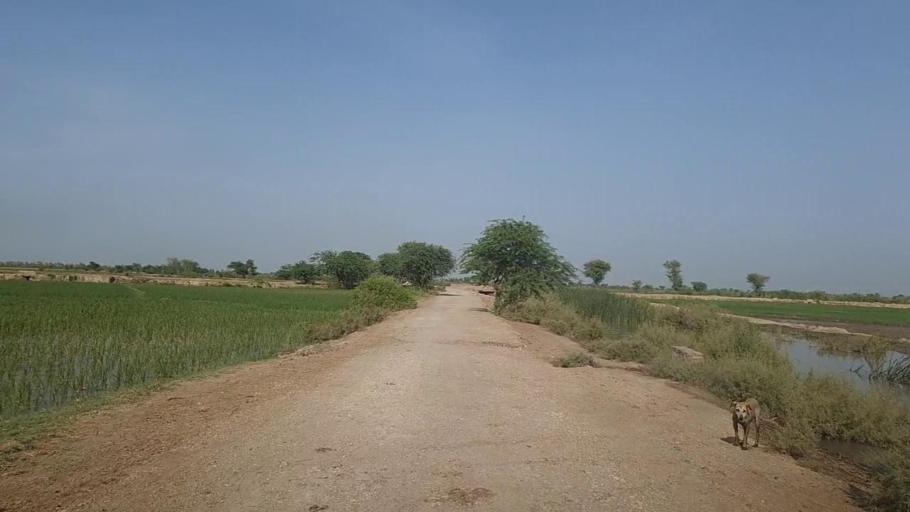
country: PK
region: Sindh
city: Sita Road
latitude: 27.0934
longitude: 67.8676
